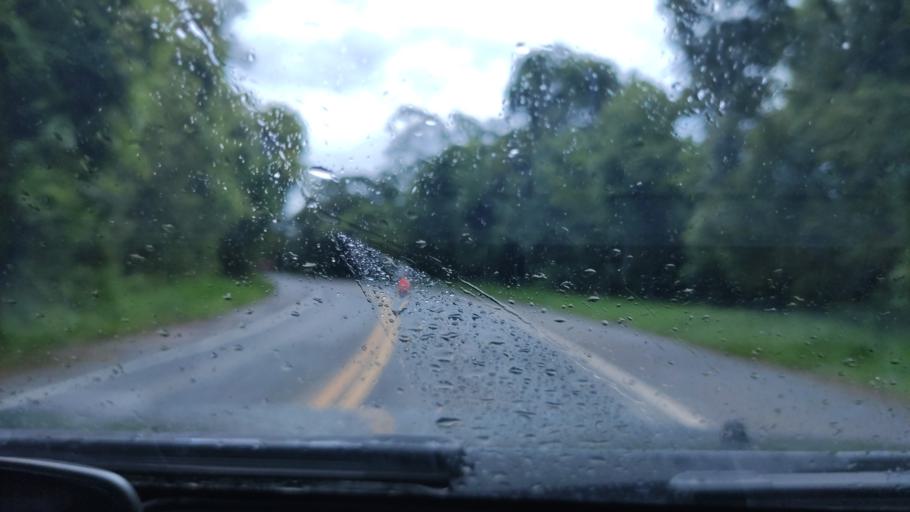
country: BR
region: Sao Paulo
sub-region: Socorro
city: Socorro
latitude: -22.7706
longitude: -46.5586
